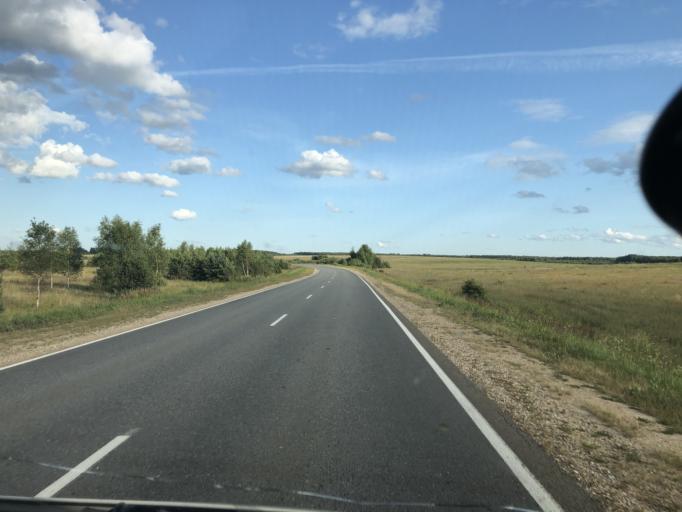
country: RU
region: Kaluga
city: Yukhnov
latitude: 54.7035
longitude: 35.2692
